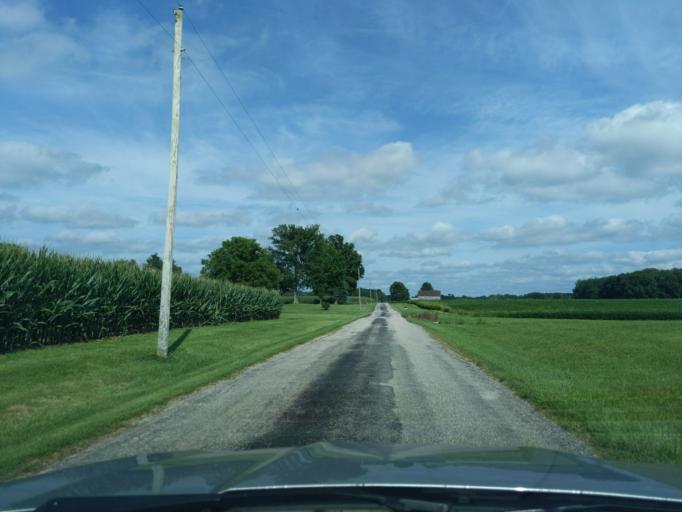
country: US
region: Indiana
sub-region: Decatur County
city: Greensburg
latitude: 39.2346
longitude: -85.4134
